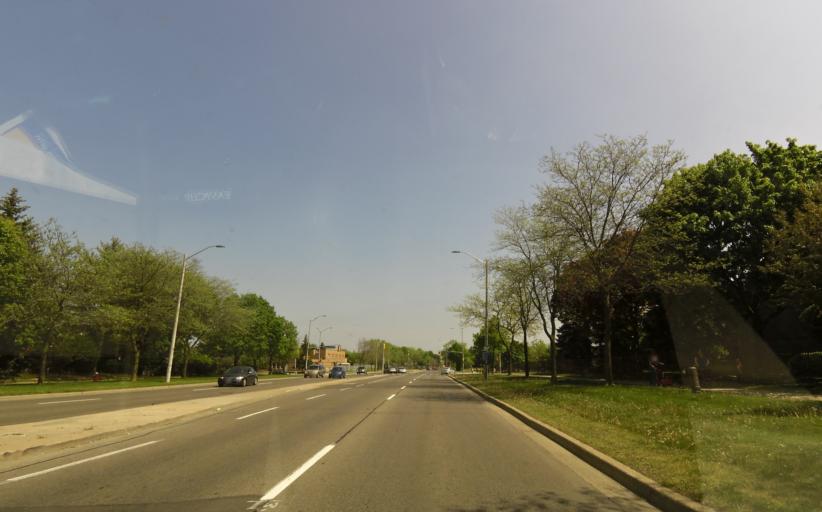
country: CA
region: Ontario
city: Mississauga
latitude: 43.5999
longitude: -79.6246
